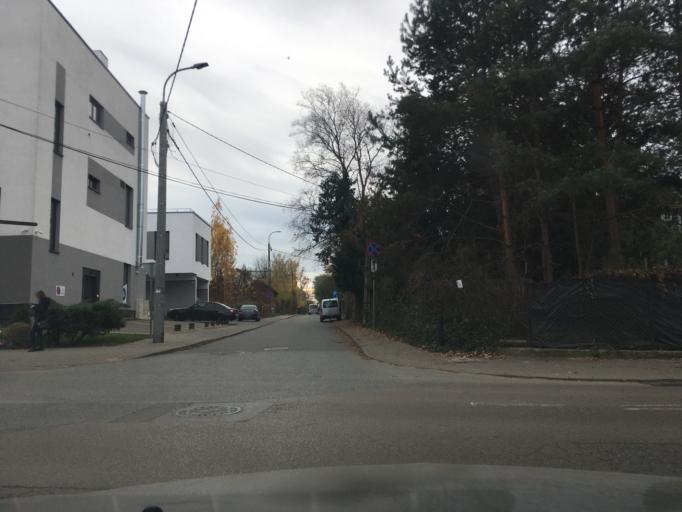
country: PL
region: Masovian Voivodeship
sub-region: Powiat piaseczynski
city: Piaseczno
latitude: 52.0726
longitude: 21.0222
